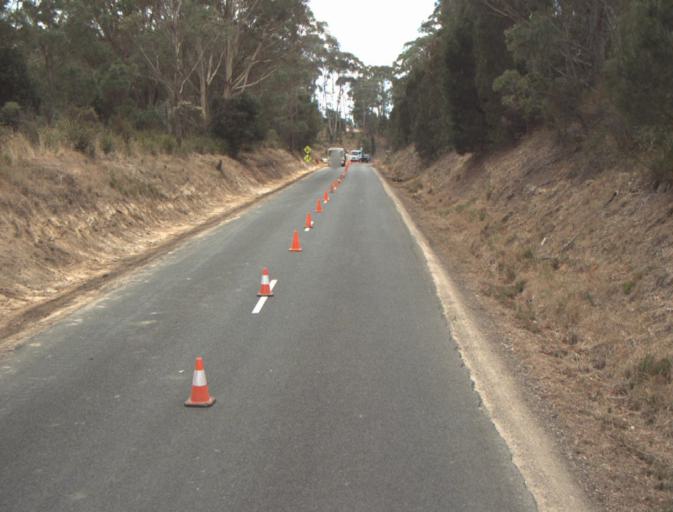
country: AU
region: Tasmania
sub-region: Launceston
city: Mayfield
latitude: -41.2326
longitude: 147.0221
